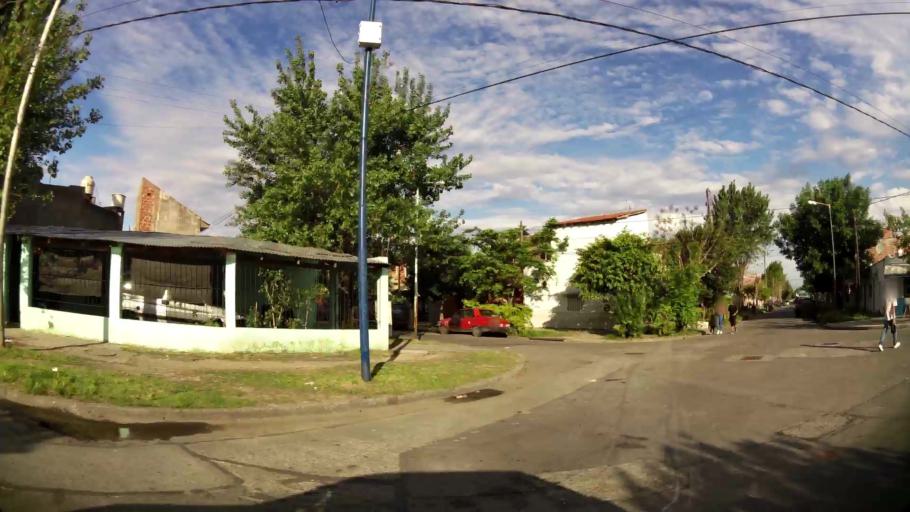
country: AR
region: Buenos Aires
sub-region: Partido de Lanus
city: Lanus
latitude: -34.7022
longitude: -58.3535
